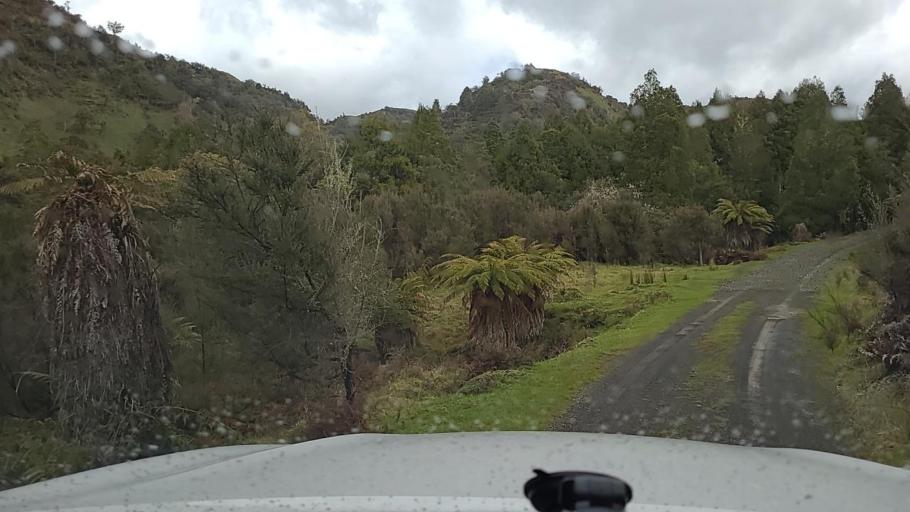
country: NZ
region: Bay of Plenty
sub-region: Opotiki District
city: Opotiki
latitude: -38.2104
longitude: 177.6074
